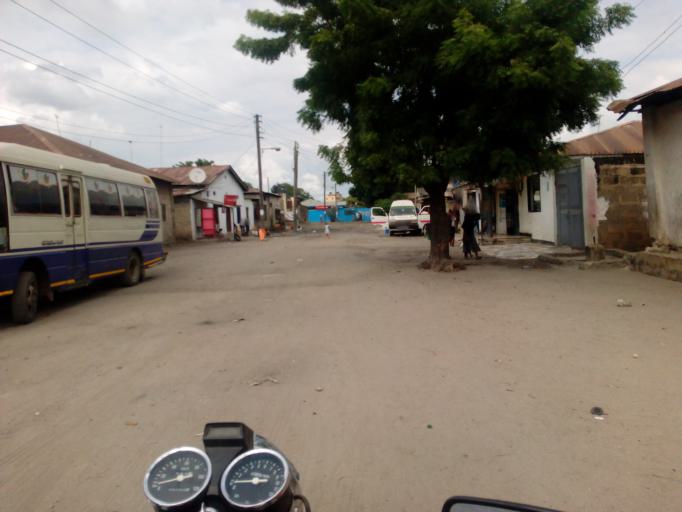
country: TZ
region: Dar es Salaam
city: Dar es Salaam
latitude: -6.8537
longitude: 39.2588
